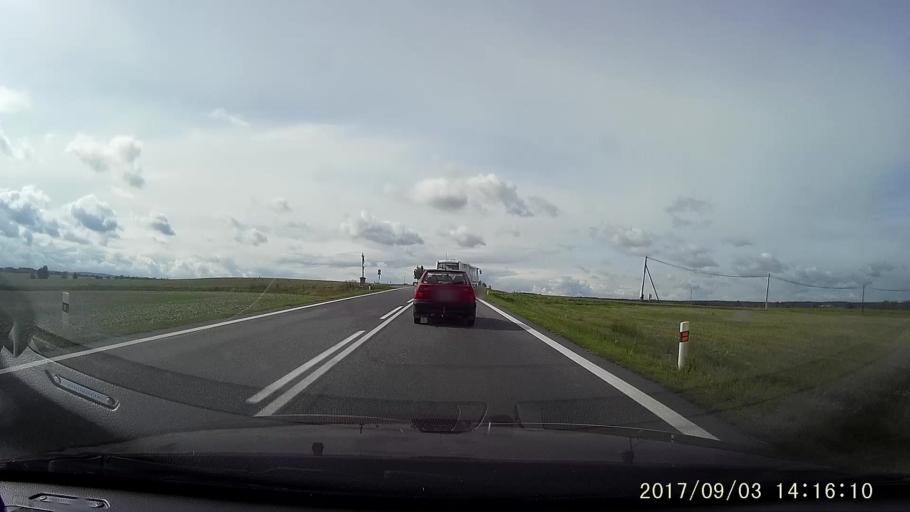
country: CZ
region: South Moravian
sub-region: Okres Znojmo
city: Znojmo
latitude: 48.8968
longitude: 15.9947
